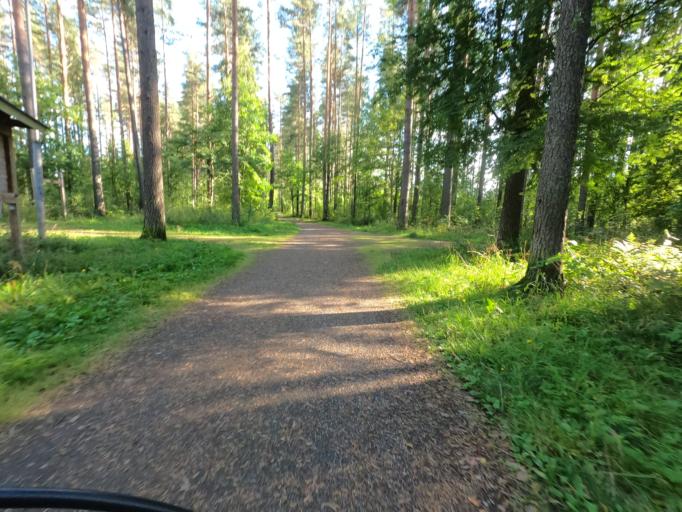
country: FI
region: North Karelia
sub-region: Joensuu
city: Joensuu
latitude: 62.6149
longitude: 29.7525
